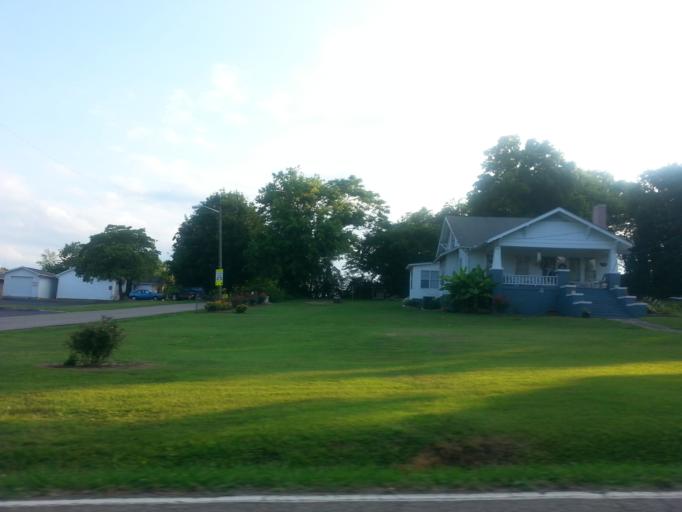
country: US
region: Tennessee
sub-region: Knox County
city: Knoxville
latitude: 36.0480
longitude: -83.9246
